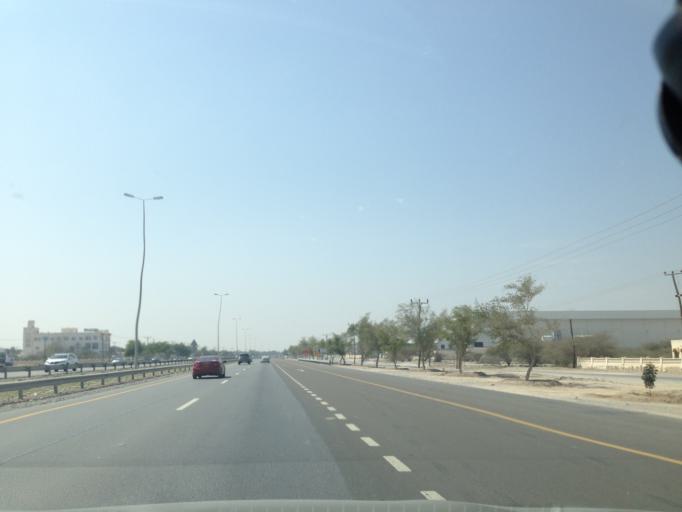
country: OM
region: Al Batinah
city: Barka'
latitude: 23.6617
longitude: 57.9426
